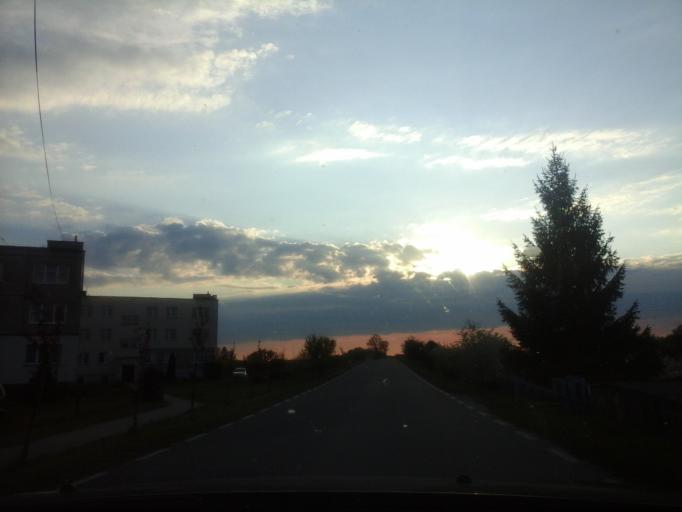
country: PL
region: West Pomeranian Voivodeship
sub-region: Powiat choszczenski
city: Krzecin
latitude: 53.0037
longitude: 15.4167
